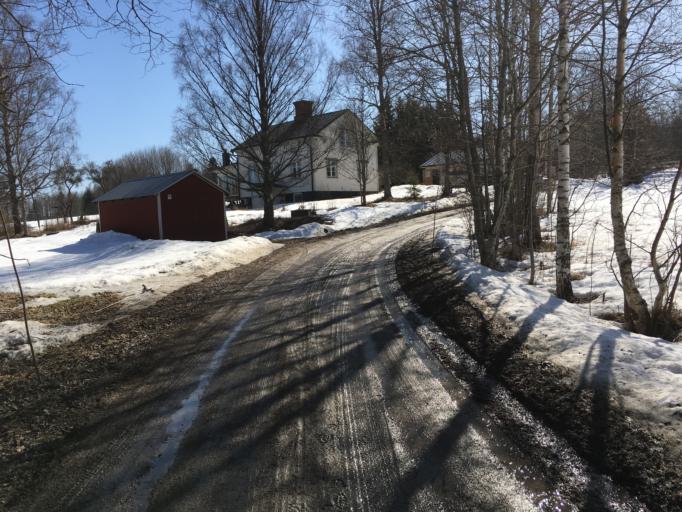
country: SE
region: Gaevleborg
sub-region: Hofors Kommun
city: Hofors
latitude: 60.5131
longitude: 16.4400
